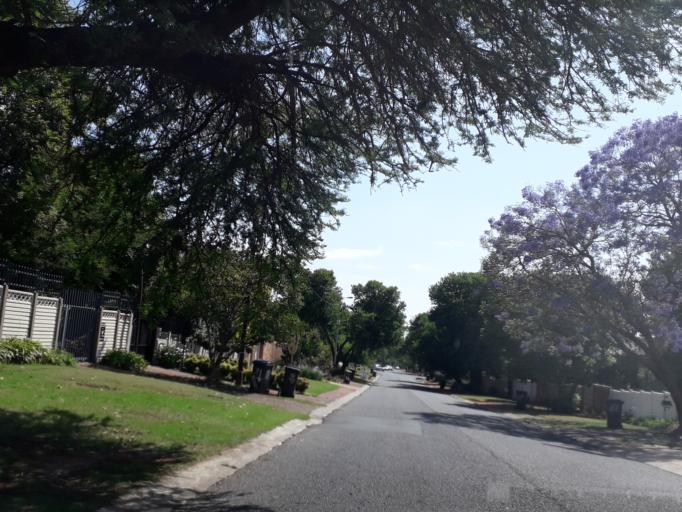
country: ZA
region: Gauteng
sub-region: City of Johannesburg Metropolitan Municipality
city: Johannesburg
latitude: -26.1092
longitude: 28.0088
